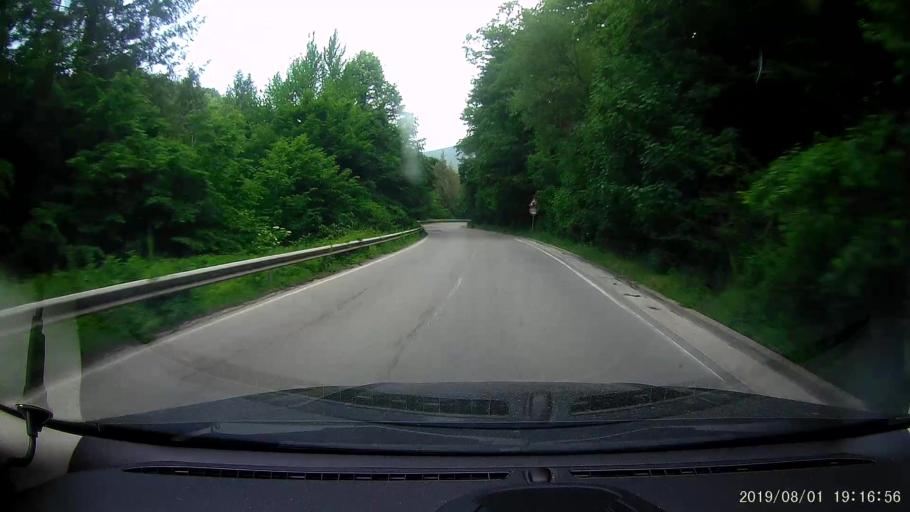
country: BG
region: Shumen
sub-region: Obshtina Smyadovo
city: Smyadovo
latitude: 42.9290
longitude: 26.9469
